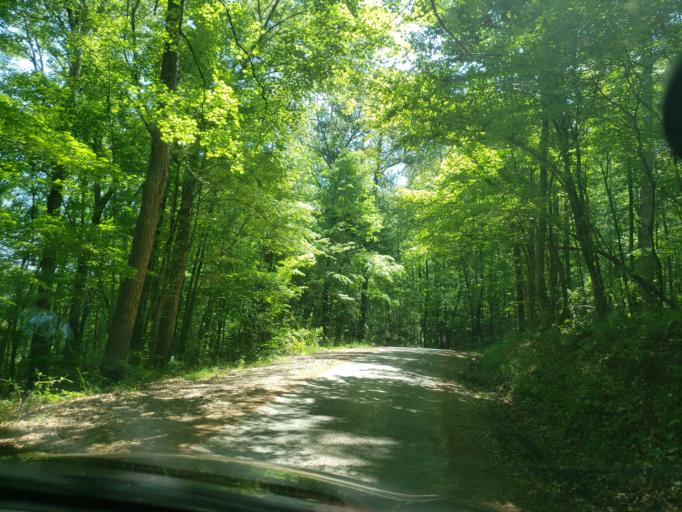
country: US
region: Alabama
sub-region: Elmore County
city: Tallassee
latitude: 32.5970
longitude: -85.8799
